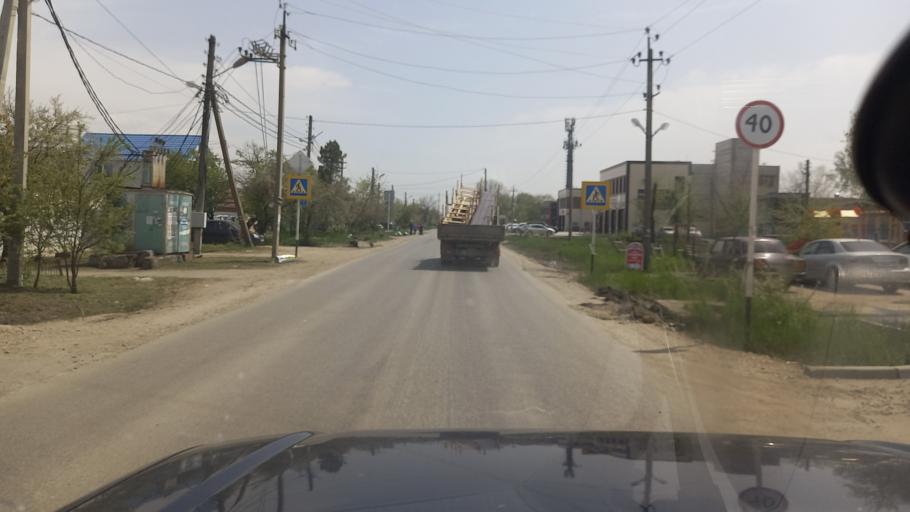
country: RU
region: Adygeya
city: Yablonovskiy
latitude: 44.9877
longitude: 38.9584
